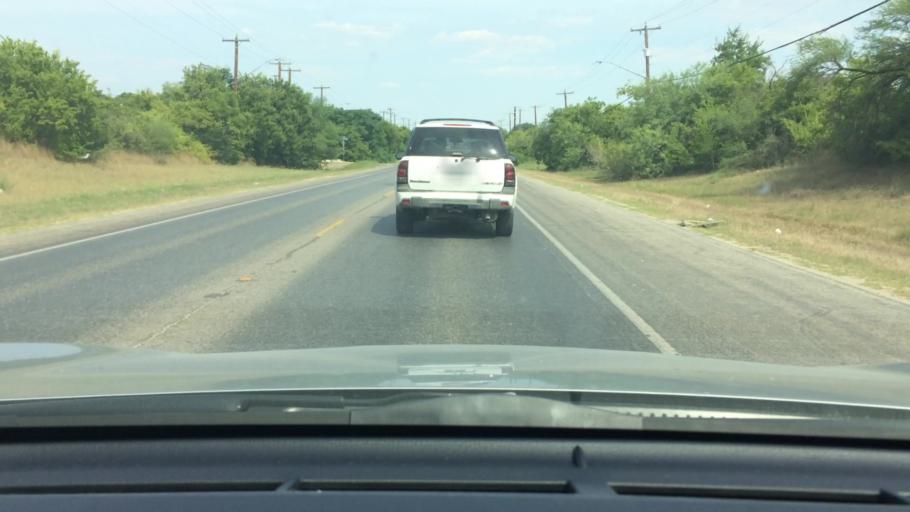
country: US
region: Texas
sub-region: Bexar County
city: San Antonio
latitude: 29.3325
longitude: -98.4478
